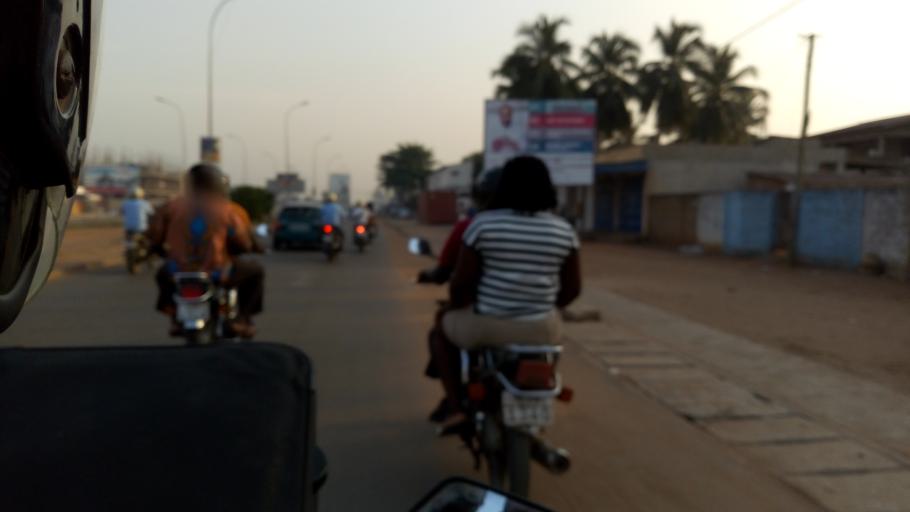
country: TG
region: Maritime
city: Lome
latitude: 6.1985
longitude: 1.1794
